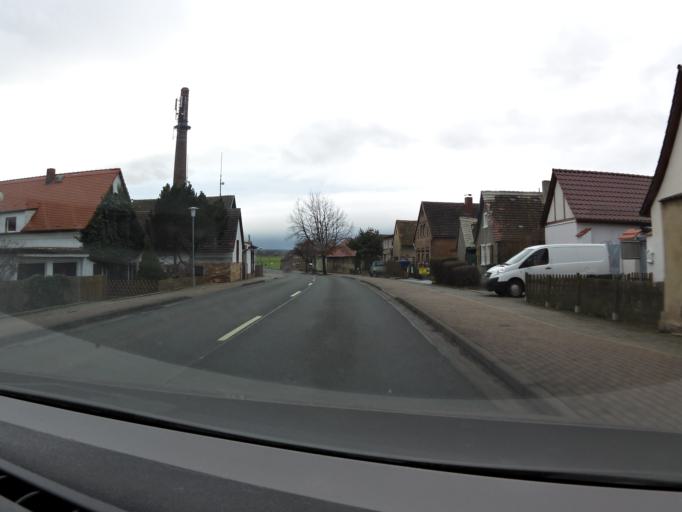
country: DE
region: Saxony-Anhalt
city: Aschersleben
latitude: 51.6953
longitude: 11.4523
